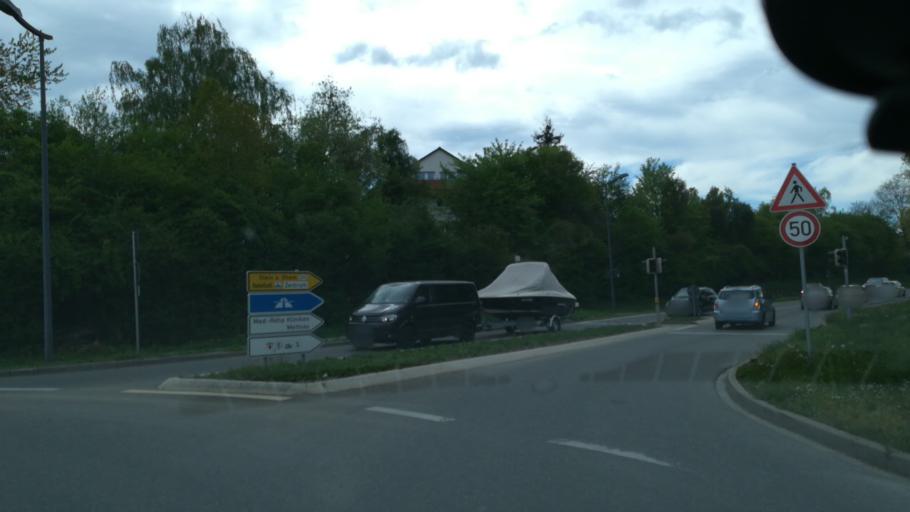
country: DE
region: Baden-Wuerttemberg
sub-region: Freiburg Region
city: Radolfzell am Bodensee
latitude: 47.7474
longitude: 8.9831
